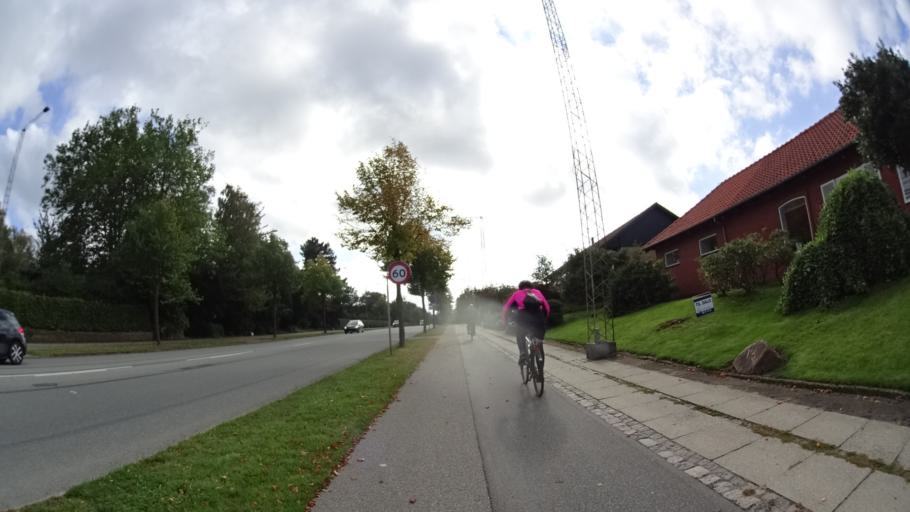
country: DK
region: Central Jutland
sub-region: Arhus Kommune
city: Arhus
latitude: 56.1297
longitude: 10.1869
